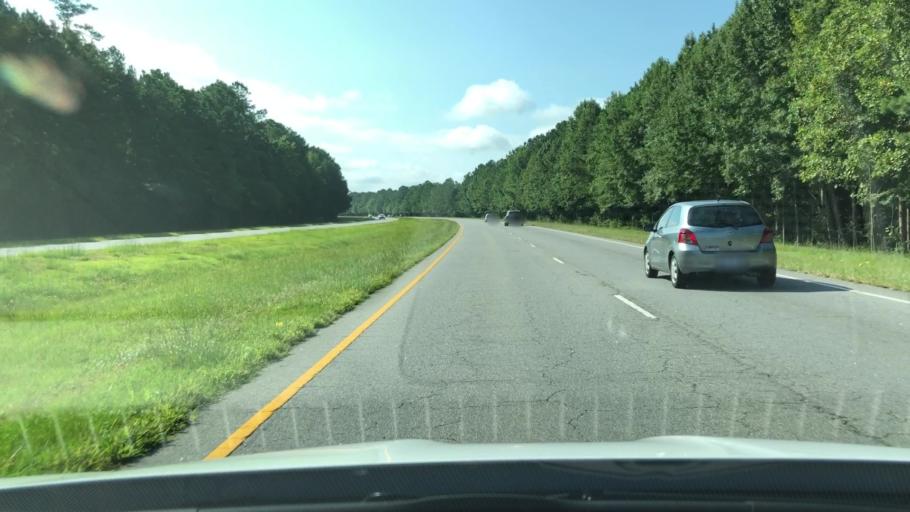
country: US
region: North Carolina
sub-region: Pasquotank County
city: Elizabeth City
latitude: 36.4087
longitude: -76.3391
